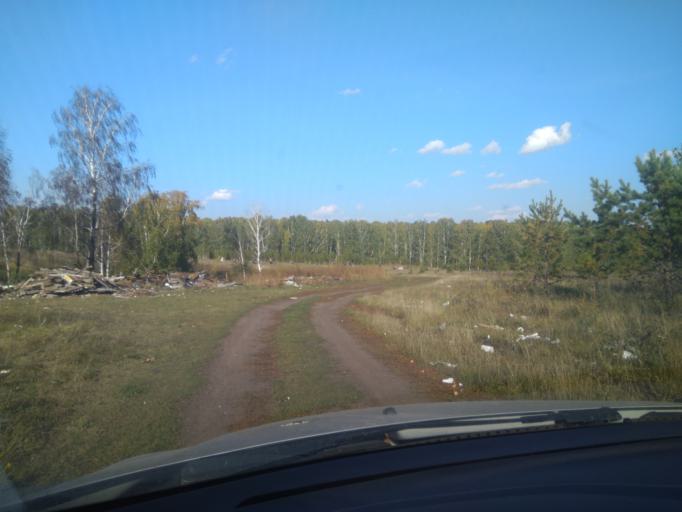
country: RU
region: Sverdlovsk
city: Pokrovskoye
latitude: 56.4260
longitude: 61.6106
